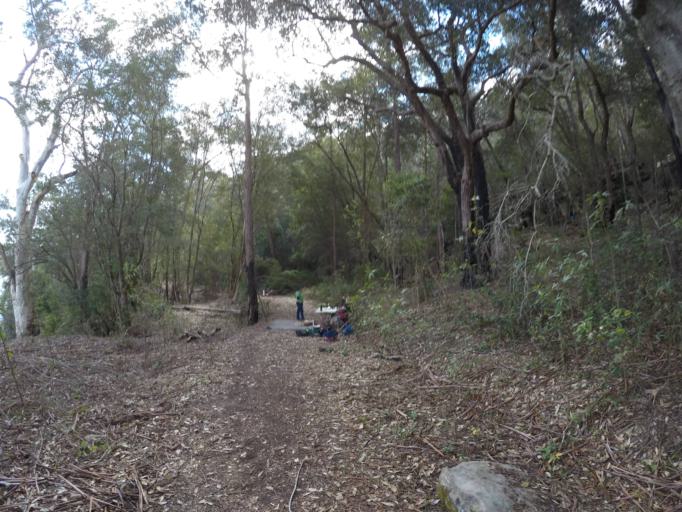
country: AU
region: New South Wales
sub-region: Hawkesbury
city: Pitt Town
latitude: -33.4710
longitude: 150.8844
